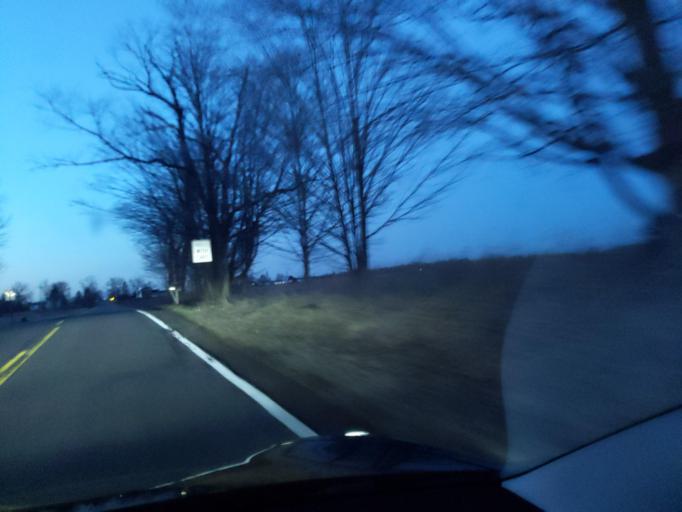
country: US
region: Michigan
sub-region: Ingham County
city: Stockbridge
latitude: 42.5456
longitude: -84.2212
